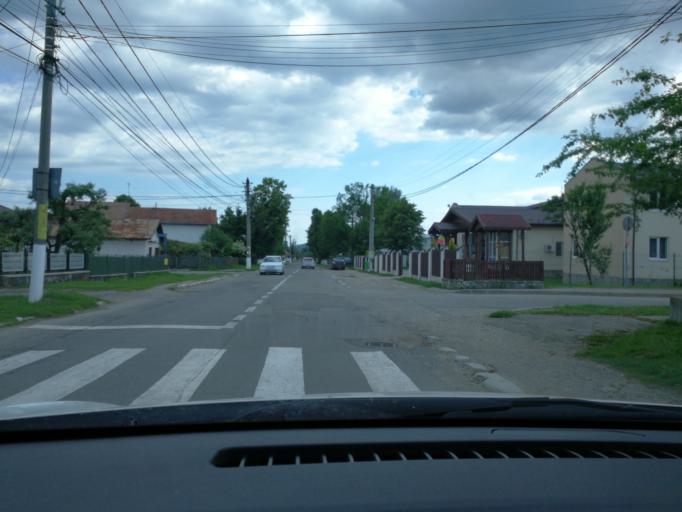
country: RO
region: Prahova
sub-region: Comuna Brebu
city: Brebu Megiesesc
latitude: 45.1483
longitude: 25.7573
